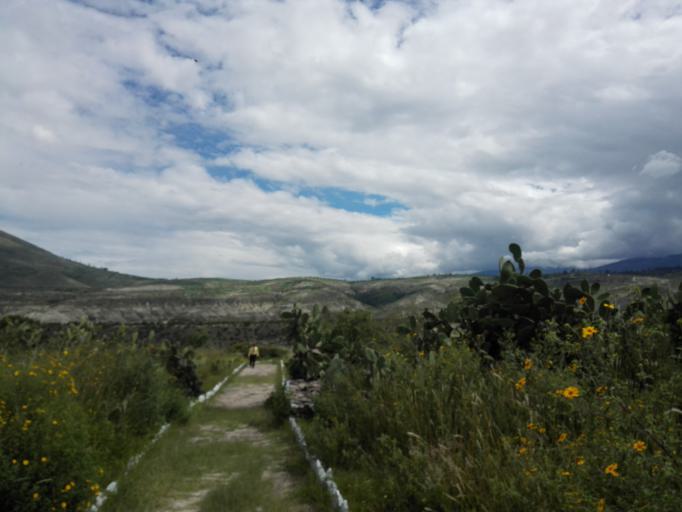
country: PE
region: Ayacucho
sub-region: Provincia de Huamanga
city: Pacaycasa
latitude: -13.0588
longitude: -74.1999
